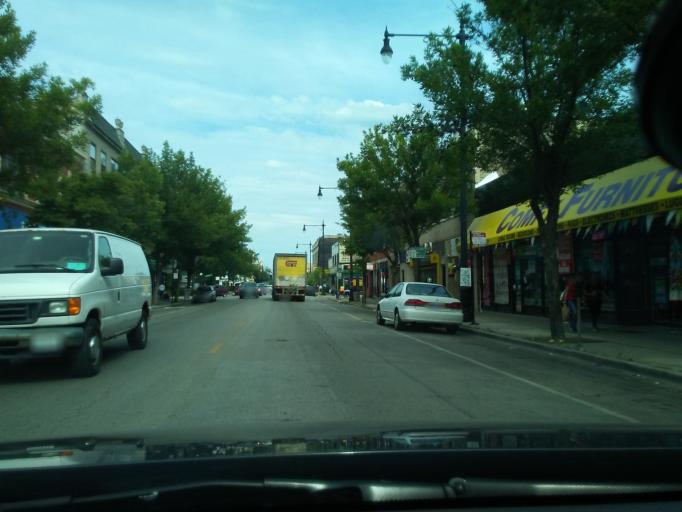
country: US
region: Illinois
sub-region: Cook County
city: Lincolnwood
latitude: 41.9684
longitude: -87.7154
